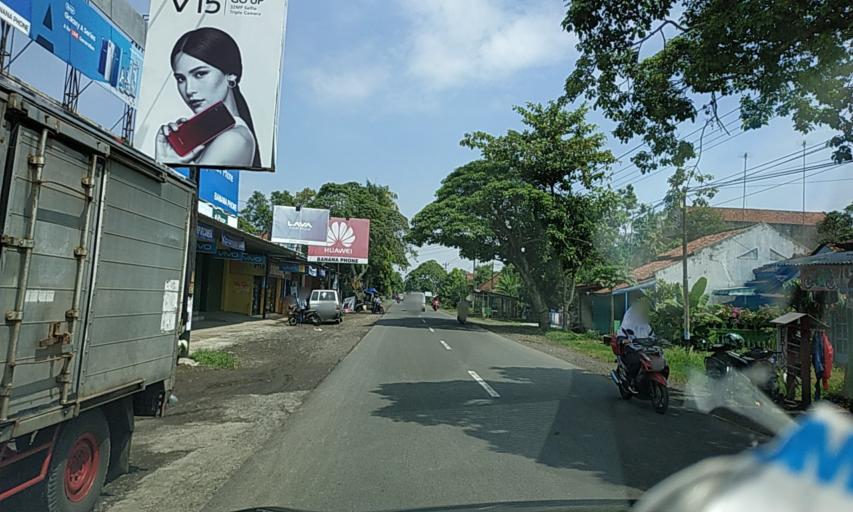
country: ID
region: Central Java
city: Gendiwu
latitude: -7.4863
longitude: 108.8135
